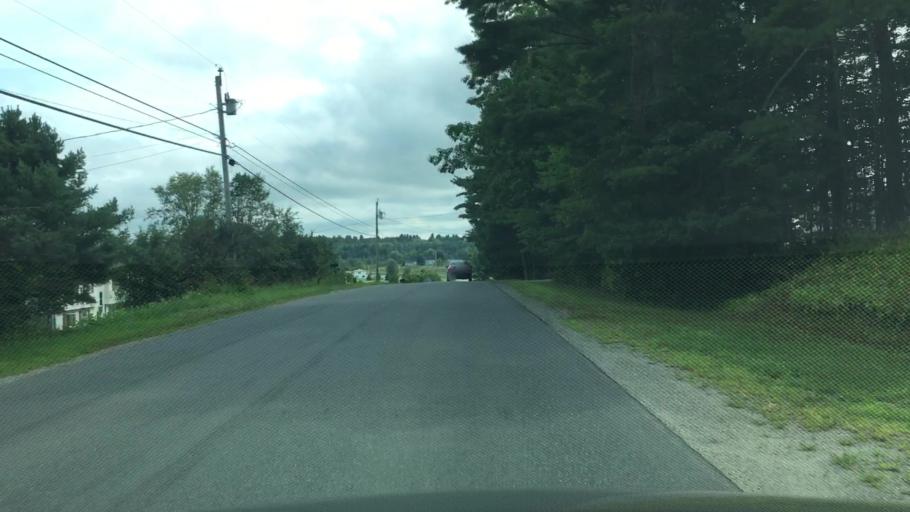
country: US
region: Maine
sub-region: Waldo County
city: Winterport
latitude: 44.6785
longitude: -68.8677
